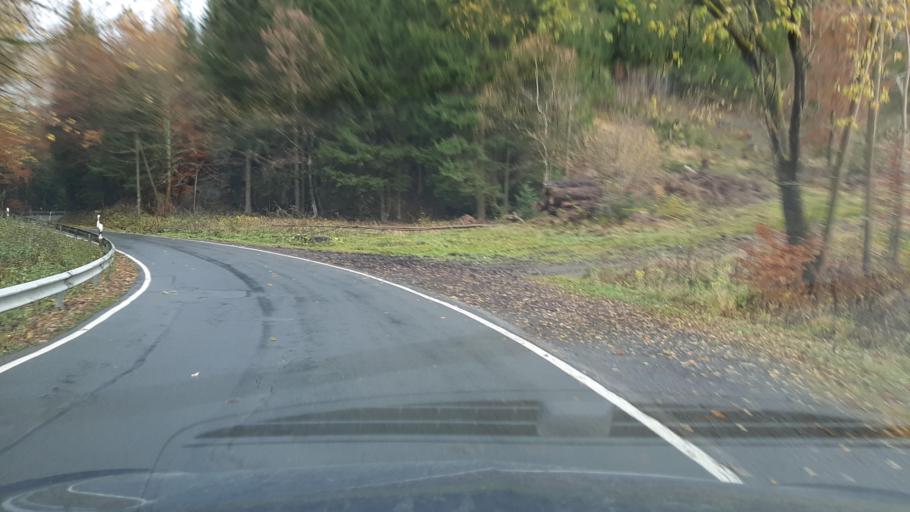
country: DE
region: North Rhine-Westphalia
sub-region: Regierungsbezirk Arnsberg
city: Winterberg
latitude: 51.2221
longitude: 8.4606
